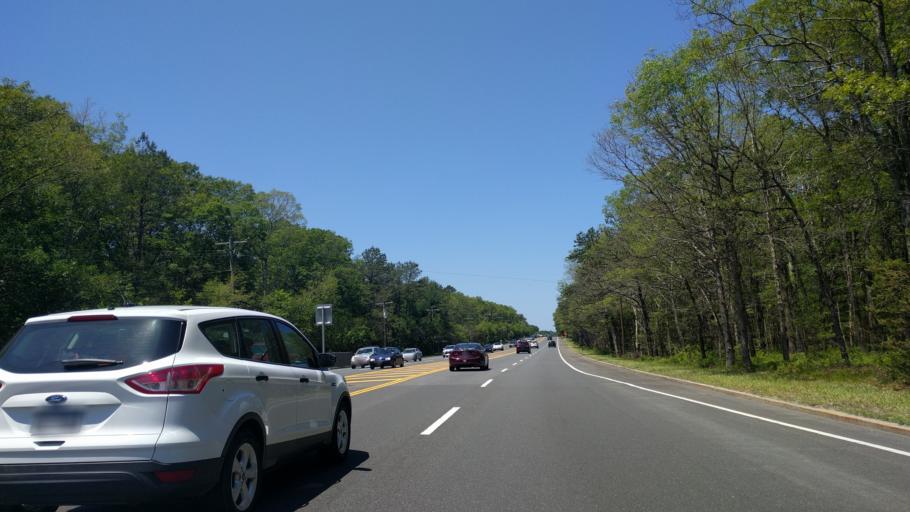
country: US
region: New York
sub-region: Suffolk County
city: Manorville
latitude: 40.8647
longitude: -72.7800
